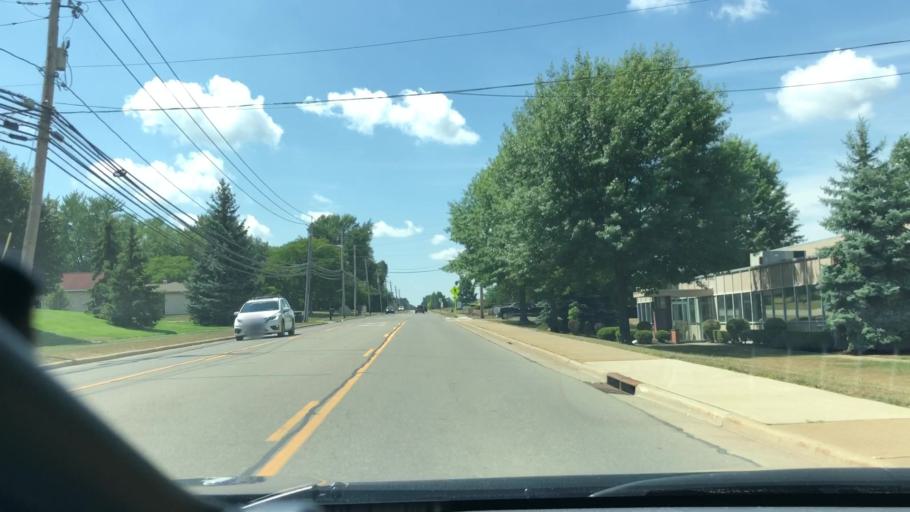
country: US
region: Ohio
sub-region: Summit County
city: Green
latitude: 40.9593
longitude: -81.4669
